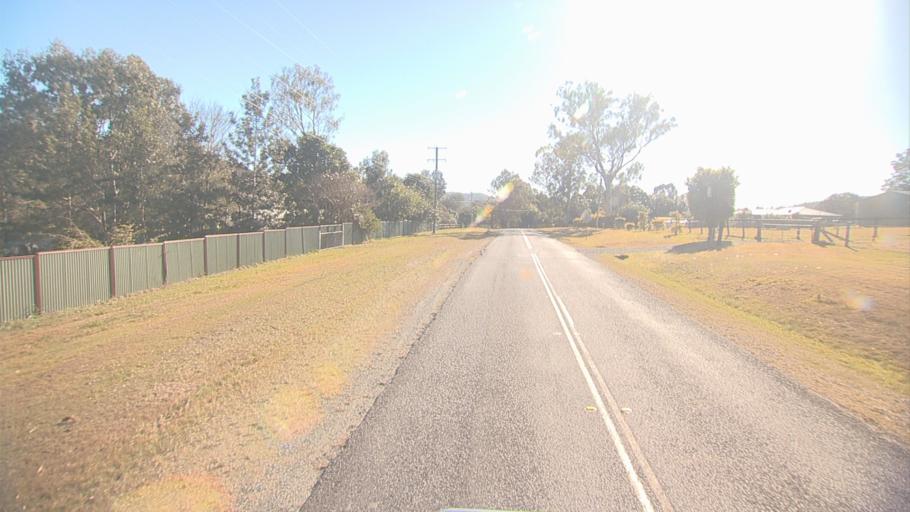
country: AU
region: Queensland
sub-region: Logan
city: Windaroo
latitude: -27.8108
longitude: 153.1706
